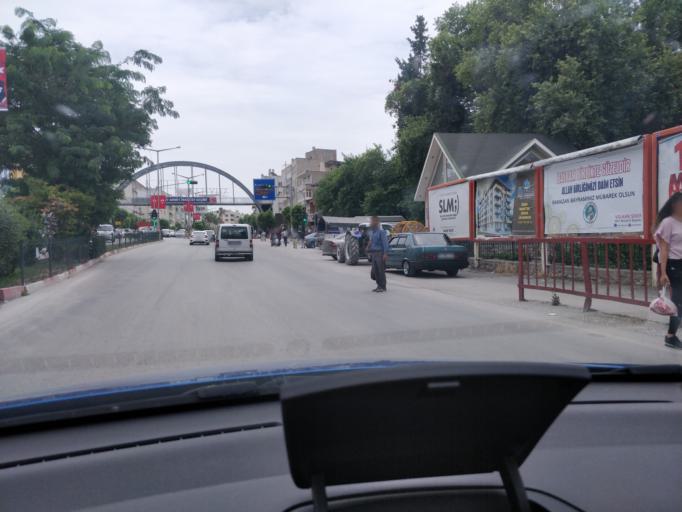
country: TR
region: Mersin
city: Mut
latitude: 36.6458
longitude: 33.4363
